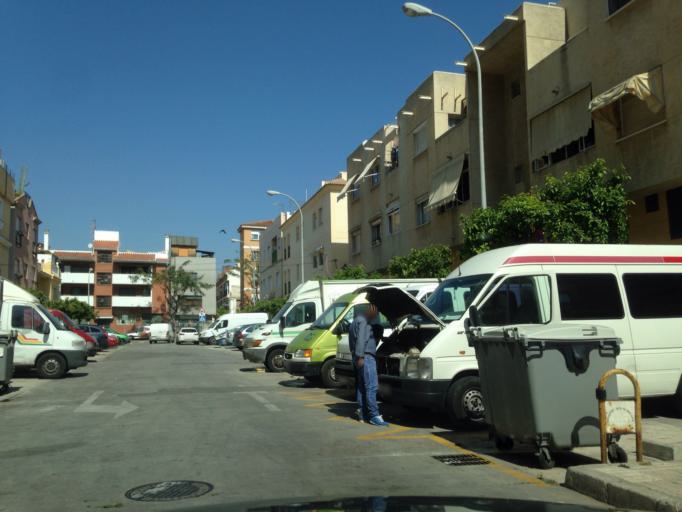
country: ES
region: Andalusia
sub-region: Provincia de Malaga
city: Malaga
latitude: 36.7013
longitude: -4.4362
